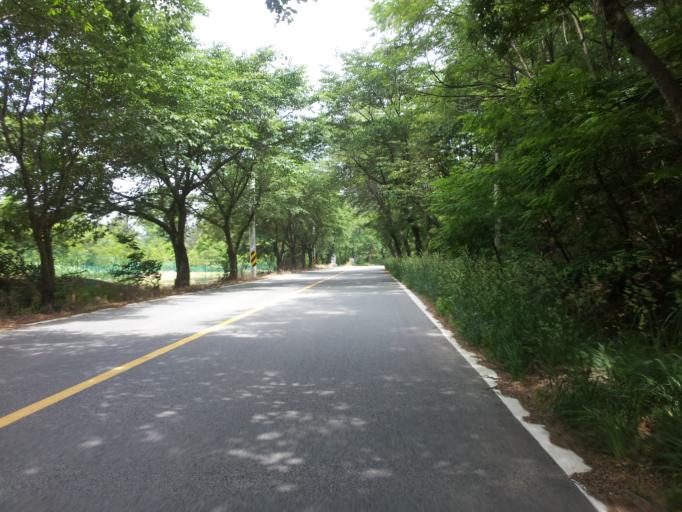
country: KR
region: Chungcheongbuk-do
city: Okcheon
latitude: 36.3832
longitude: 127.5187
